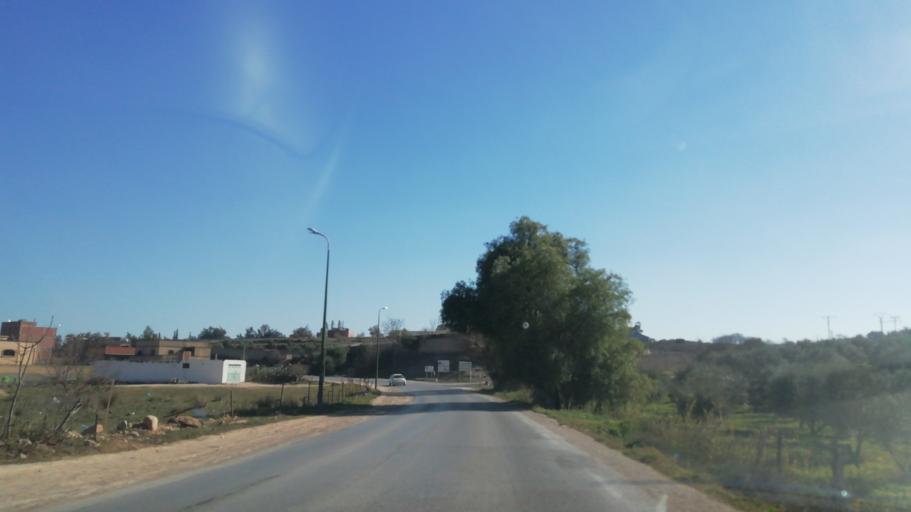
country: DZ
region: Tlemcen
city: Nedroma
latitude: 34.8406
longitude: -1.7100
